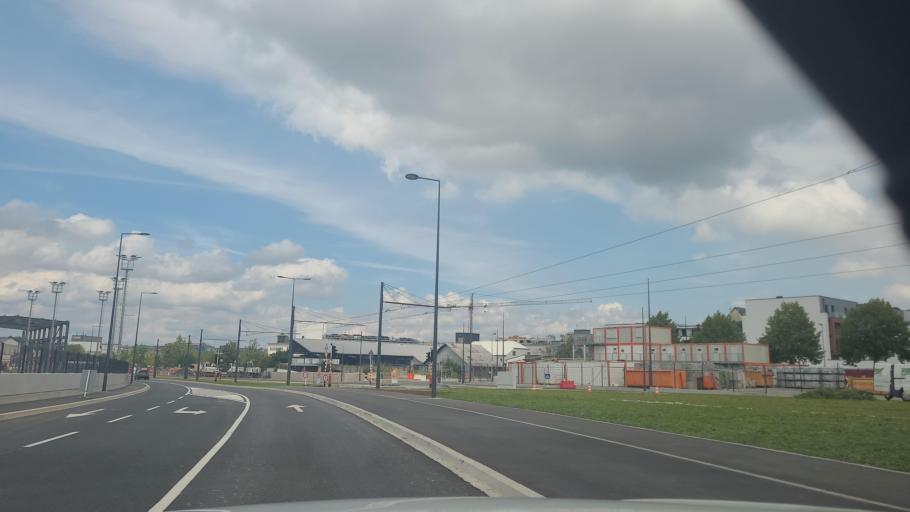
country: LU
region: Luxembourg
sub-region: Canton de Luxembourg
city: Luxembourg
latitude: 49.5906
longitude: 6.1380
